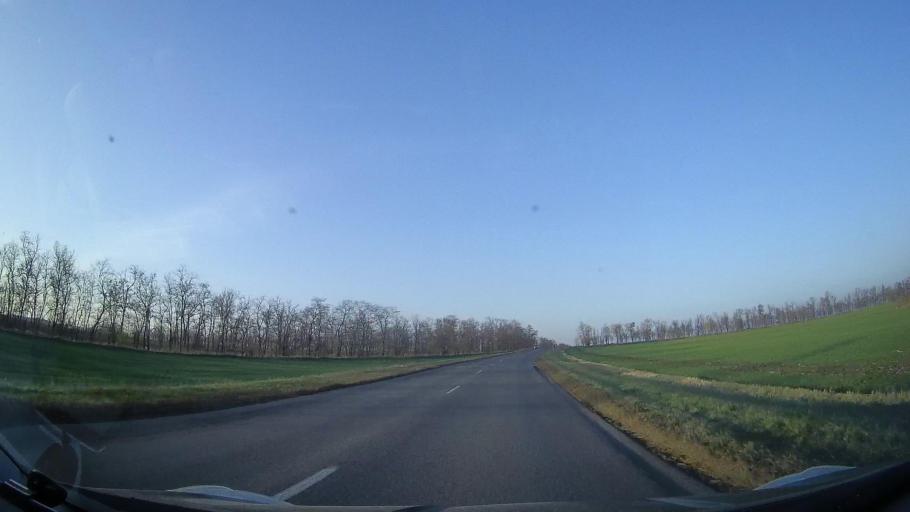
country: RU
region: Rostov
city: Kirovskaya
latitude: 47.0375
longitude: 39.9789
